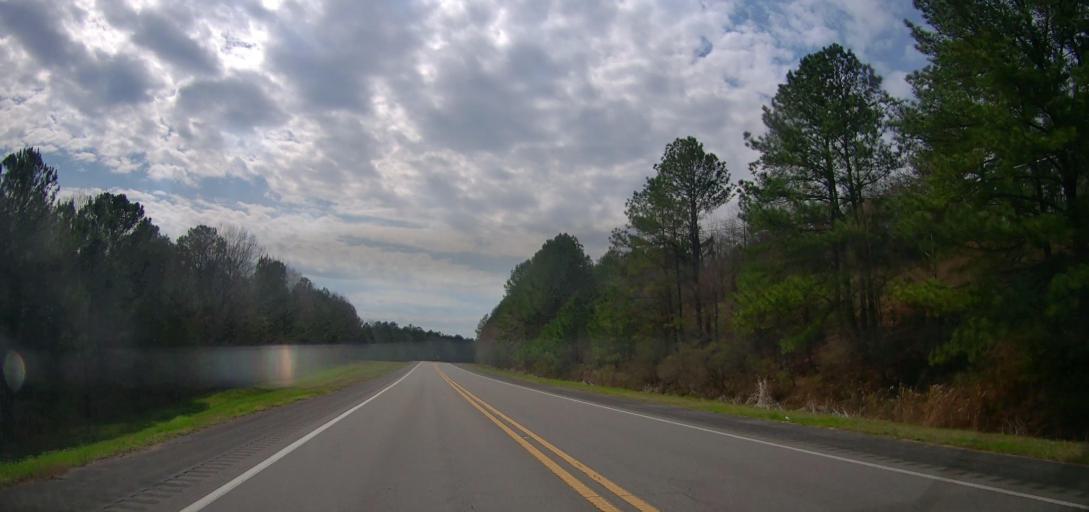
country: US
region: Alabama
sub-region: Walker County
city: Carbon Hill
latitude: 33.9300
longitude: -87.6691
